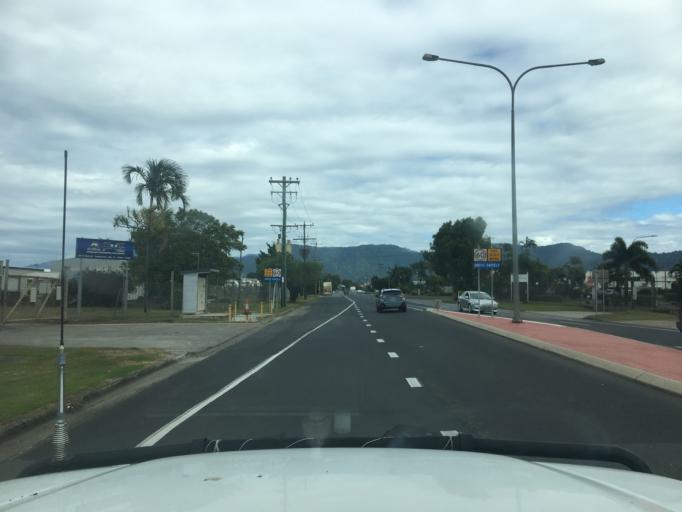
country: AU
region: Queensland
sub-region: Cairns
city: Cairns
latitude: -16.9339
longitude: 145.7722
